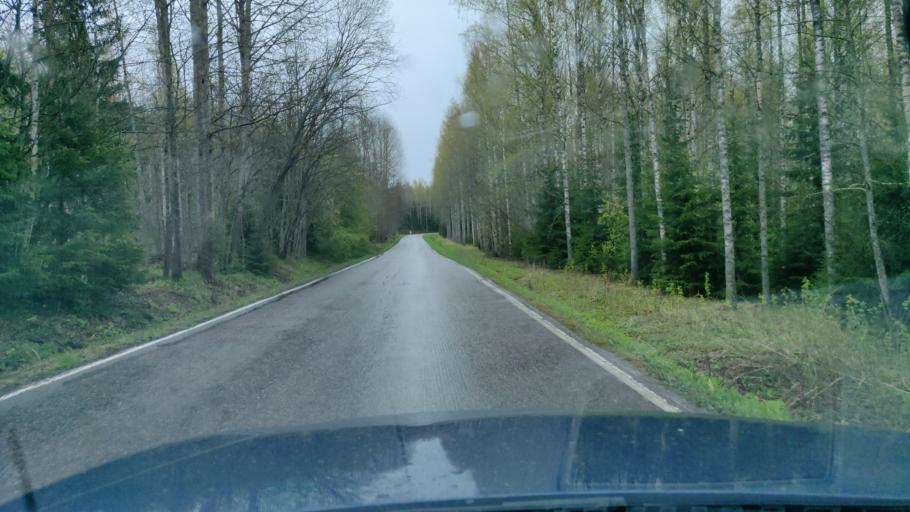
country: FI
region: Uusimaa
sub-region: Helsinki
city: Nurmijaervi
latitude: 60.5000
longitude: 24.7099
